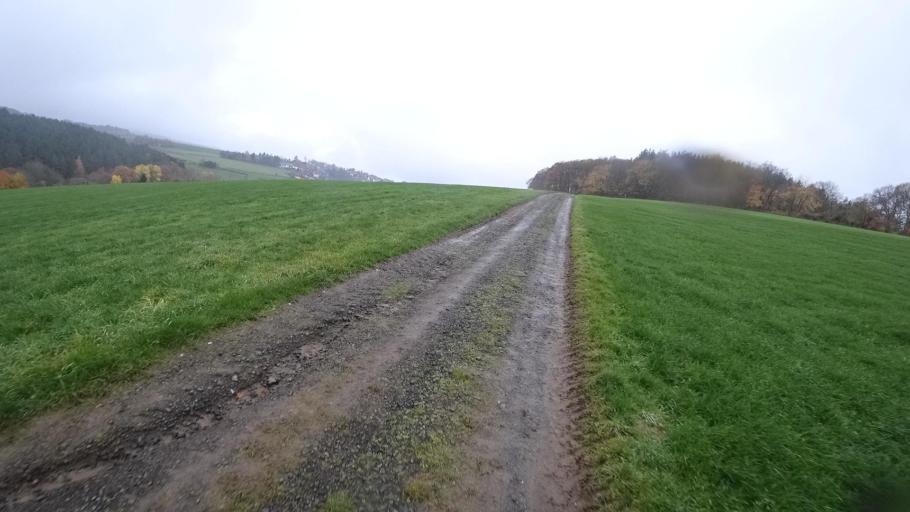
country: DE
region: Rheinland-Pfalz
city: Bad Neuenahr-Ahrweiler
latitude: 50.4961
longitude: 7.0965
